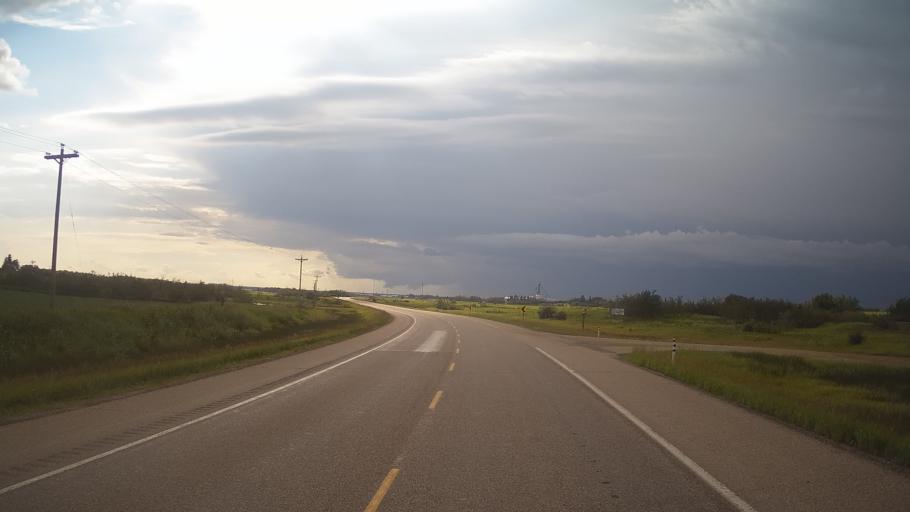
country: CA
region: Alberta
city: Vegreville
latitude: 53.2211
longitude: -112.2067
